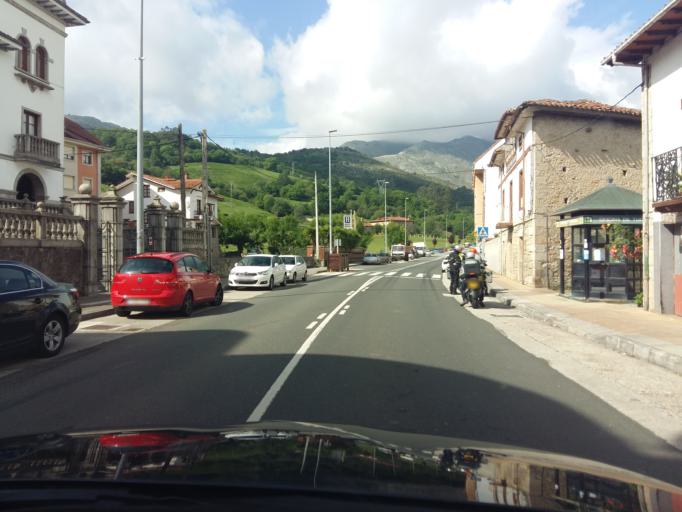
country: ES
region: Cantabria
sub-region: Provincia de Cantabria
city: Tresviso
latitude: 43.3228
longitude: -4.5851
